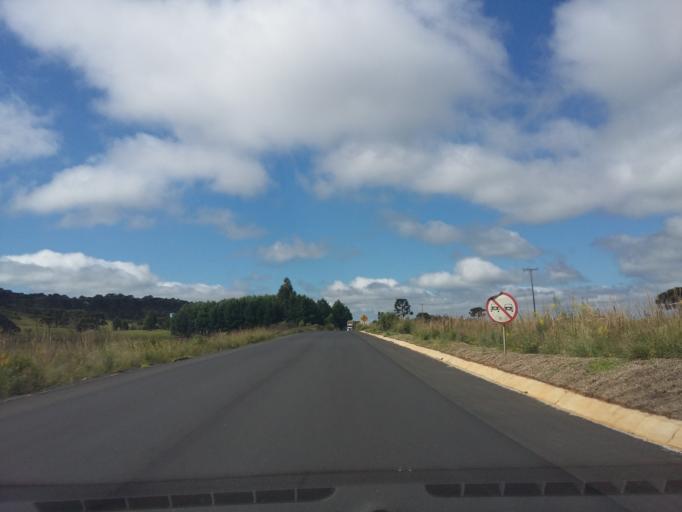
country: BR
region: Santa Catarina
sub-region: Sao Joaquim
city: Sao Joaquim
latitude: -28.0397
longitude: -50.0735
